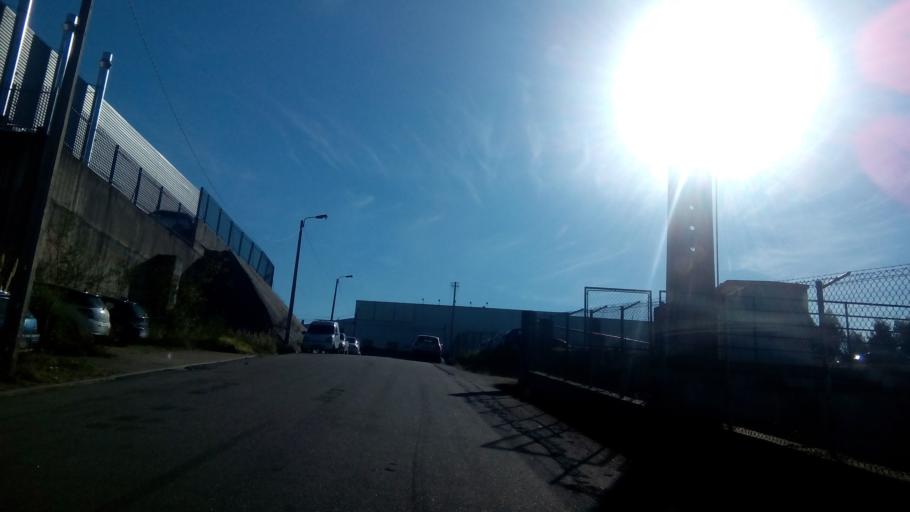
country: PT
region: Porto
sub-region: Paredes
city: Gandra
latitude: 41.1917
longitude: -8.4142
